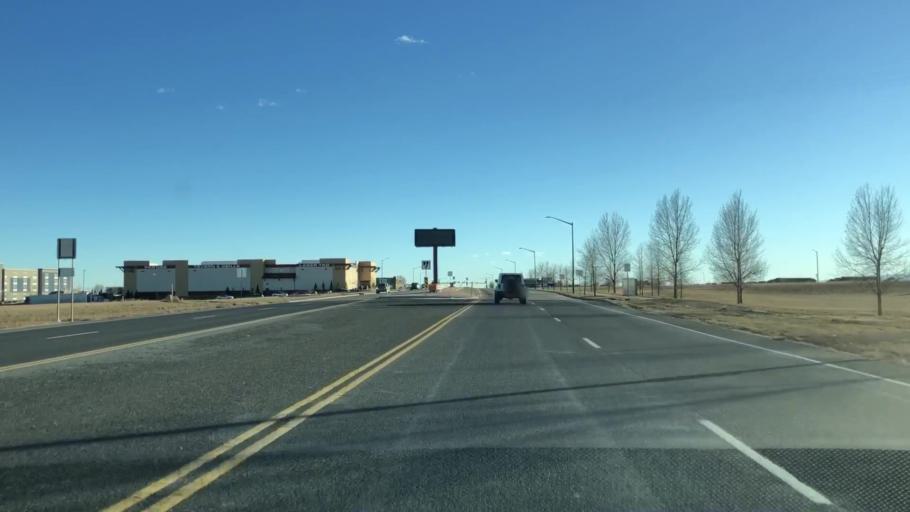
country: US
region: Colorado
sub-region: Weld County
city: Windsor
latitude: 40.4411
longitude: -104.9826
